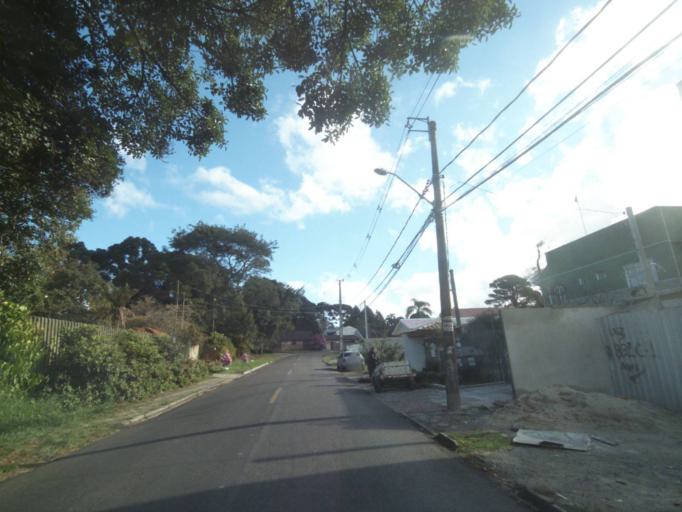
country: BR
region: Parana
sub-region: Sao Jose Dos Pinhais
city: Sao Jose dos Pinhais
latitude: -25.5287
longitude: -49.2849
